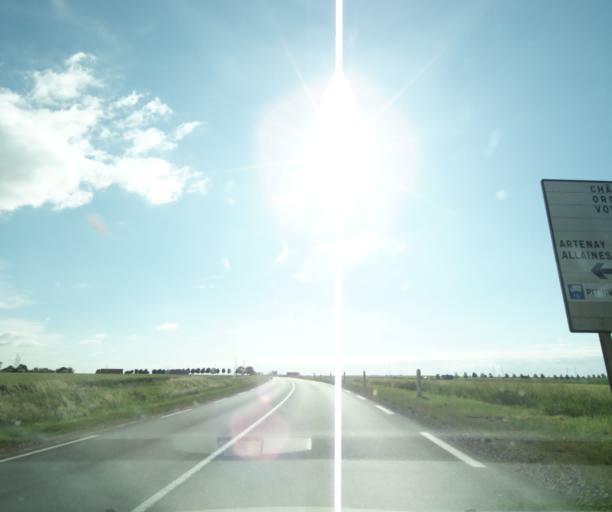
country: FR
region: Centre
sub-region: Departement d'Eure-et-Loir
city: Janville
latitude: 48.2080
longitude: 1.8252
